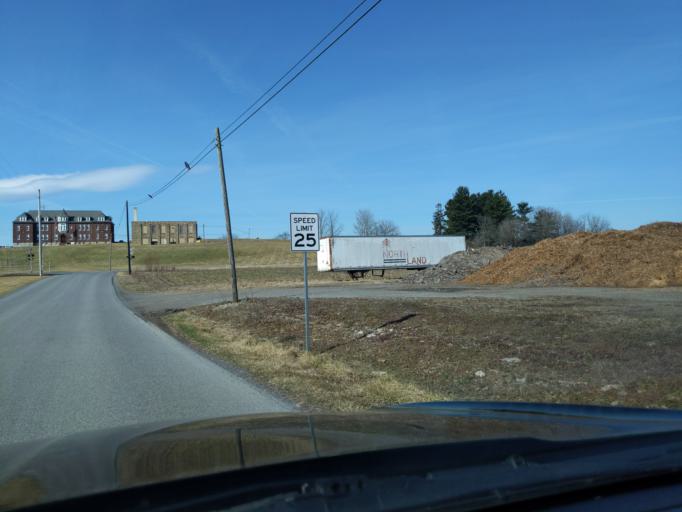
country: US
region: Pennsylvania
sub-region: Blair County
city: Martinsburg
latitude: 40.3094
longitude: -78.3381
